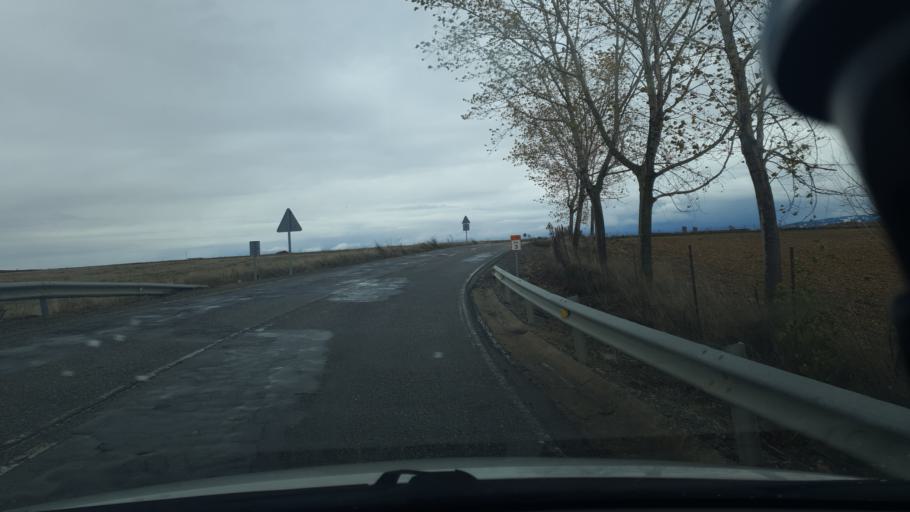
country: ES
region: Castille and Leon
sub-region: Provincia de Segovia
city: Segovia
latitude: 40.9678
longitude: -4.1406
